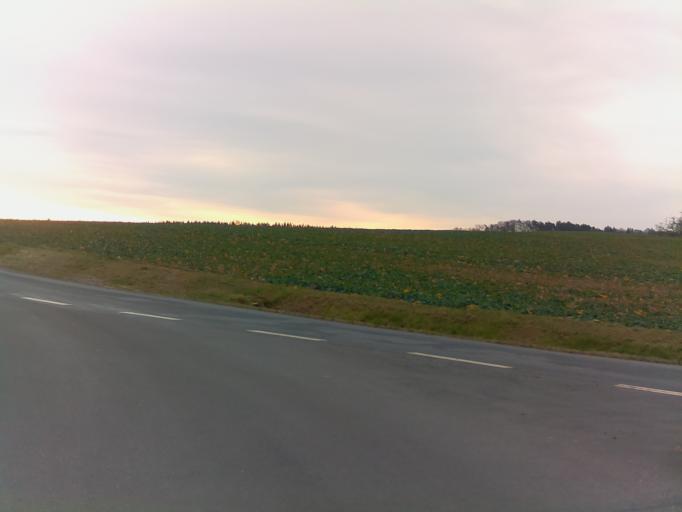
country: DE
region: Thuringia
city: Hundhaupten
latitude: 50.8320
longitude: 11.9950
